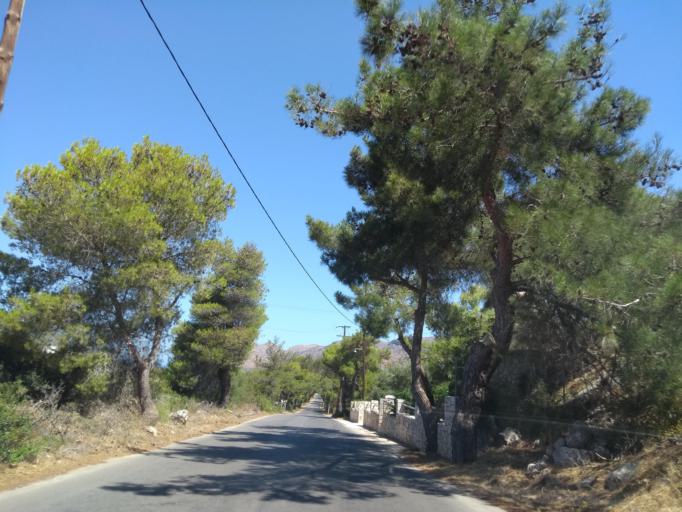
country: GR
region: Crete
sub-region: Nomos Chanias
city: Mouzouras
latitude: 35.5504
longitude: 24.1285
